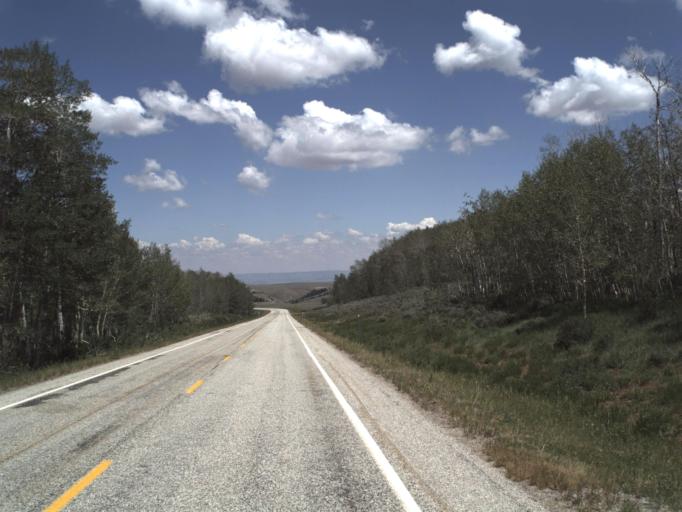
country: US
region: Utah
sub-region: Rich County
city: Randolph
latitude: 41.4733
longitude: -111.4463
